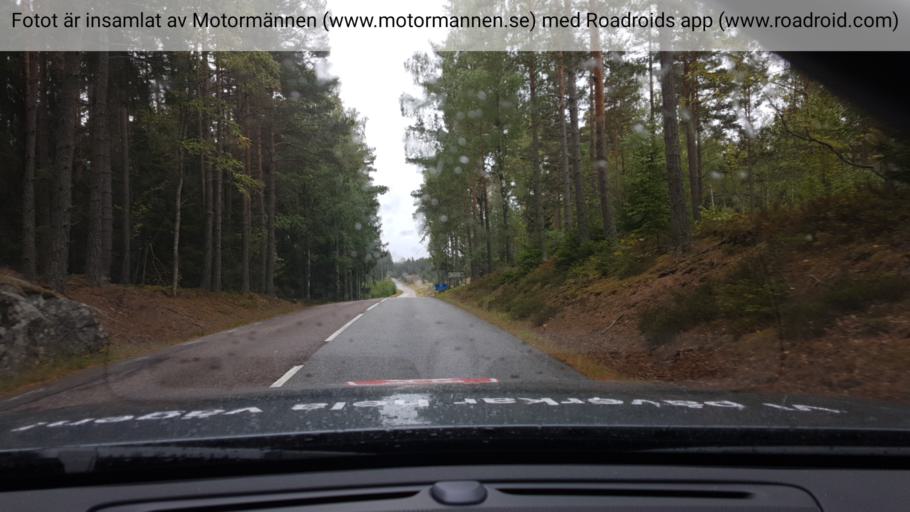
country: SE
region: Stockholm
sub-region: Botkyrka Kommun
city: Tullinge
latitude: 59.0953
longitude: 17.8890
